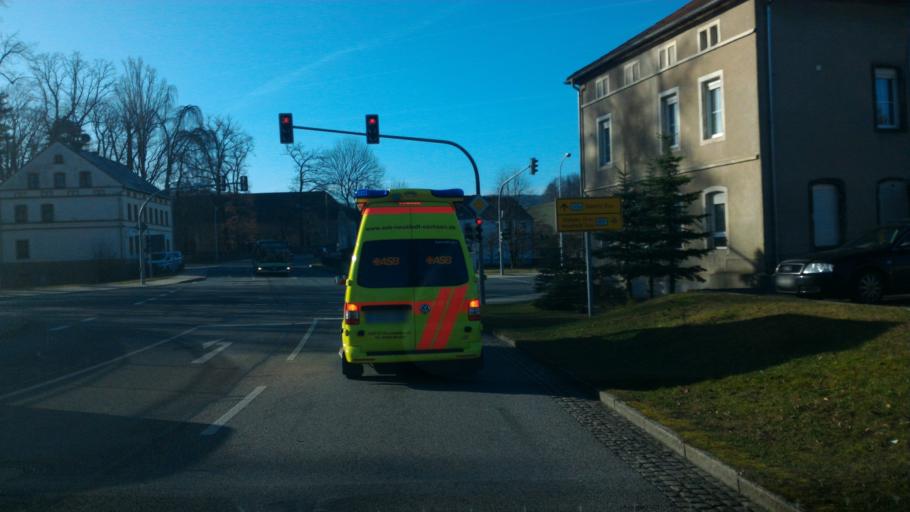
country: DE
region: Saxony
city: Neustadt in Sachsen
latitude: 51.0247
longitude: 14.2324
